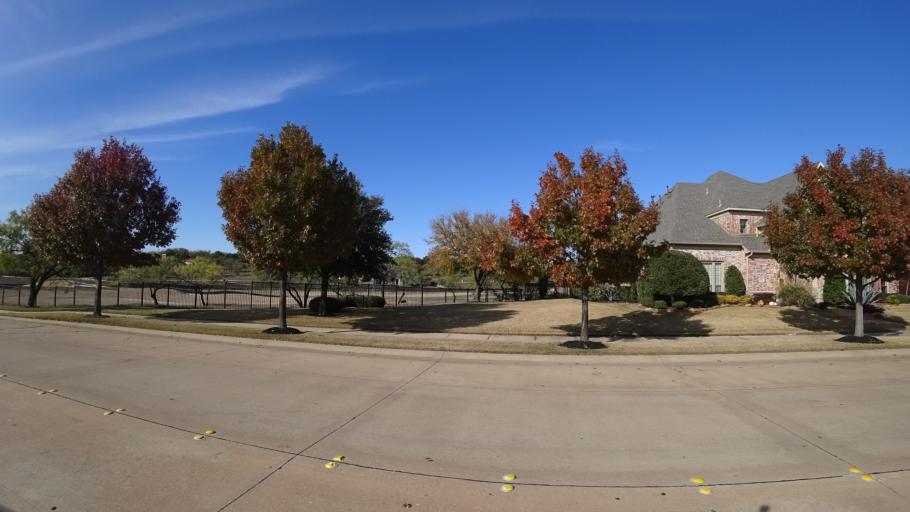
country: US
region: Texas
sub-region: Denton County
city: The Colony
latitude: 33.0308
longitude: -96.9047
